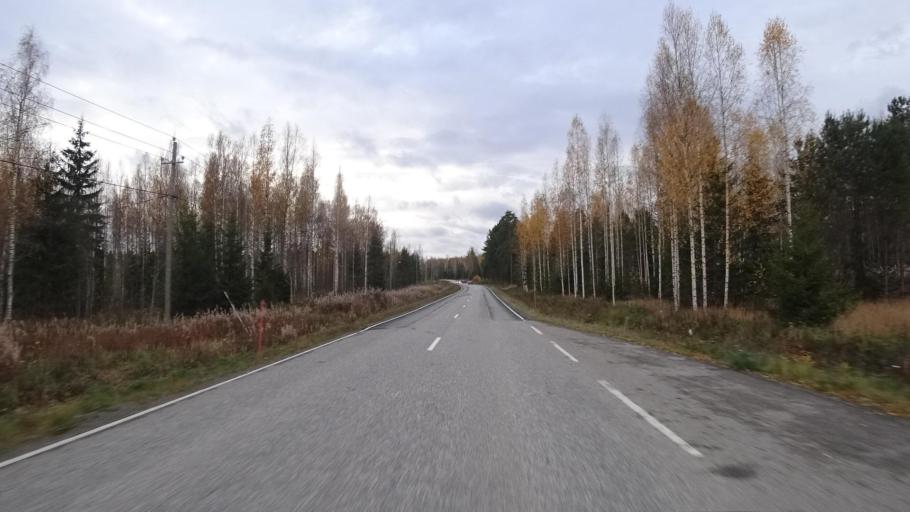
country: FI
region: Central Finland
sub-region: Joutsa
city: Joutsa
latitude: 61.8036
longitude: 26.1840
